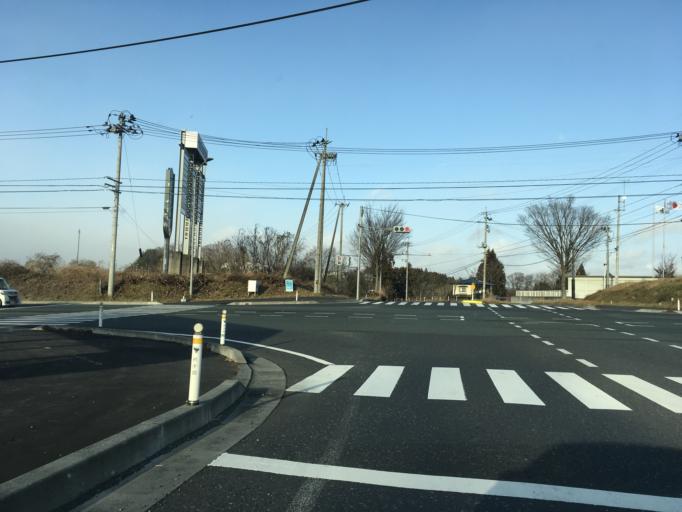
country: JP
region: Iwate
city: Ichinoseki
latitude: 38.9115
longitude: 141.1590
